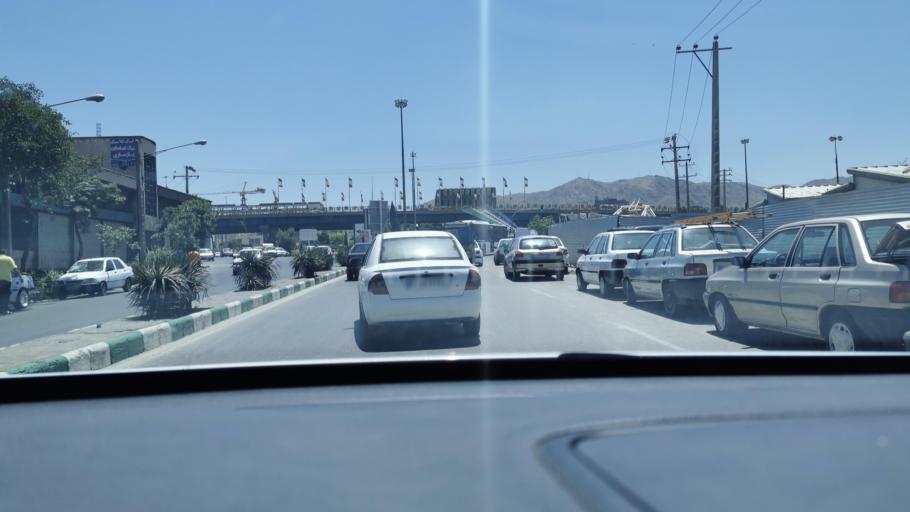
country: IR
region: Razavi Khorasan
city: Mashhad
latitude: 36.2574
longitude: 59.6002
